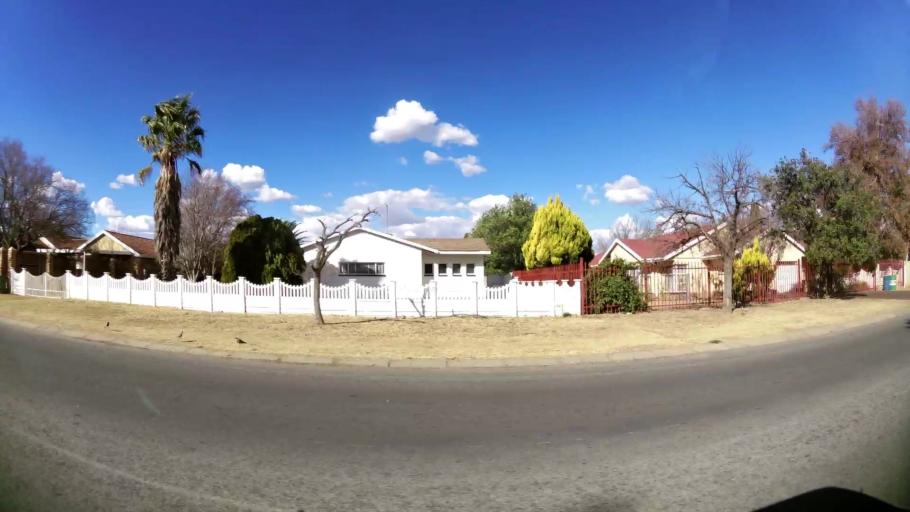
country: ZA
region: North-West
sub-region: Dr Kenneth Kaunda District Municipality
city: Klerksdorp
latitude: -26.8350
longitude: 26.6558
